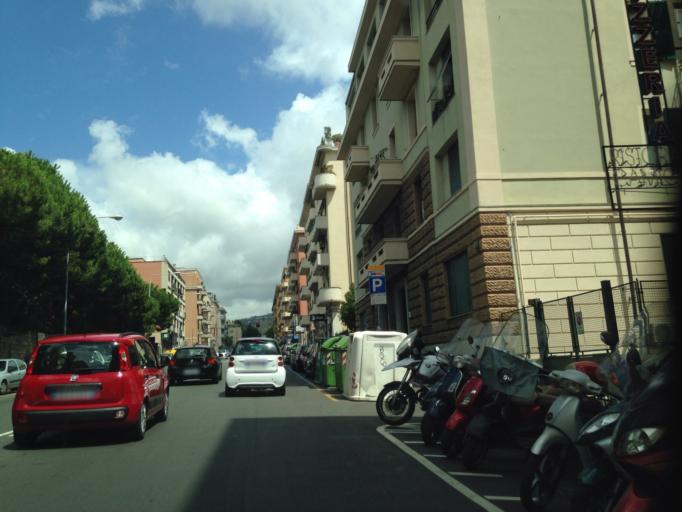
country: IT
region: Liguria
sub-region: Provincia di Genova
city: San Teodoro
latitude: 44.3920
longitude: 8.9746
